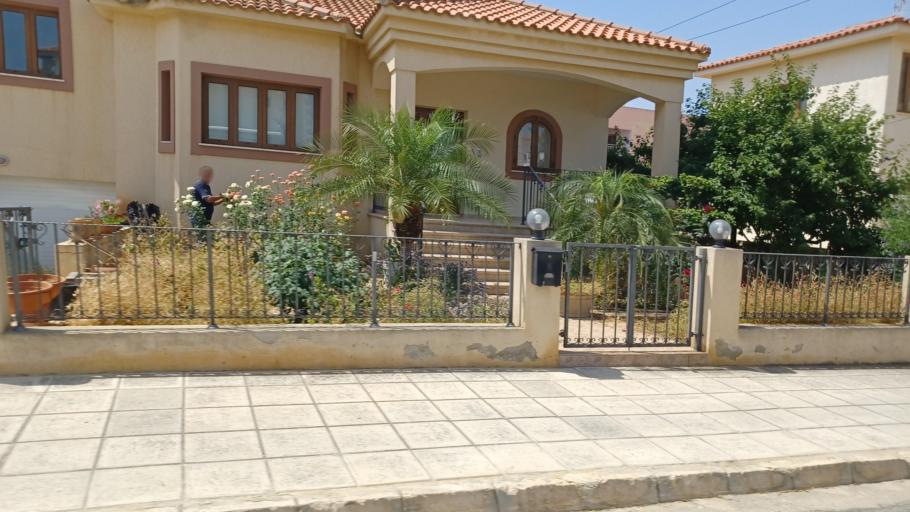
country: CY
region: Ammochostos
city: Paralimni
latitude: 35.0507
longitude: 33.9815
